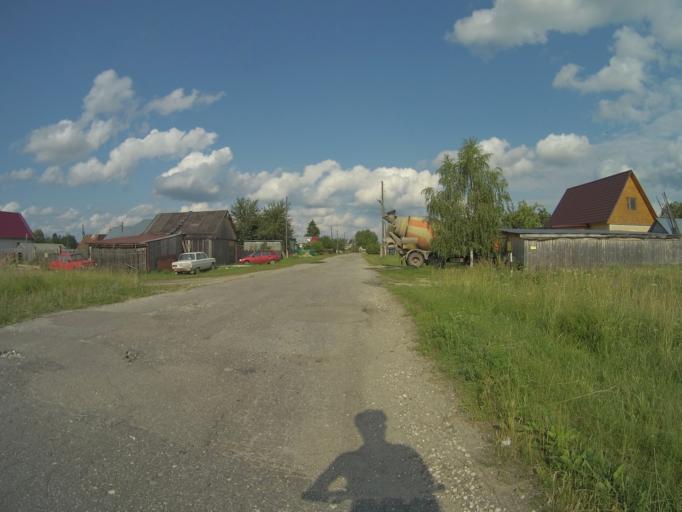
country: RU
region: Vladimir
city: Orgtrud
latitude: 56.2856
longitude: 40.7717
